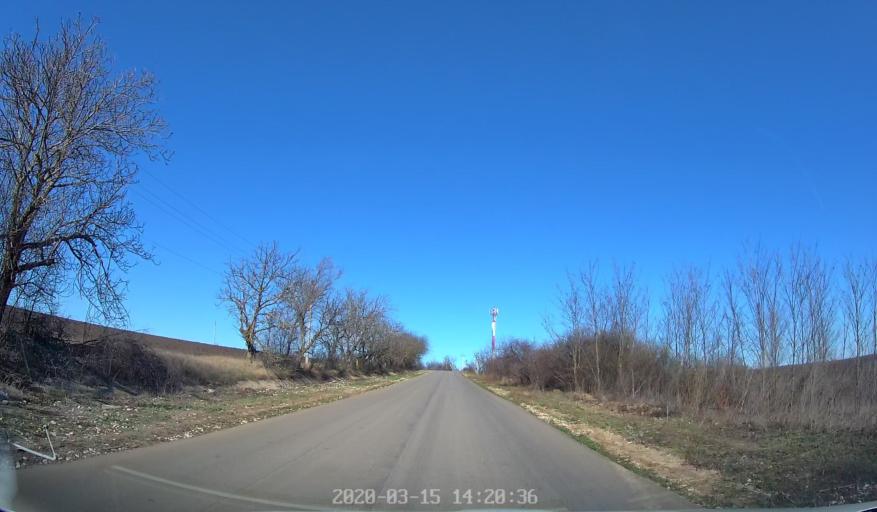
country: MD
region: Orhei
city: Orhei
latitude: 47.3111
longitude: 28.9231
